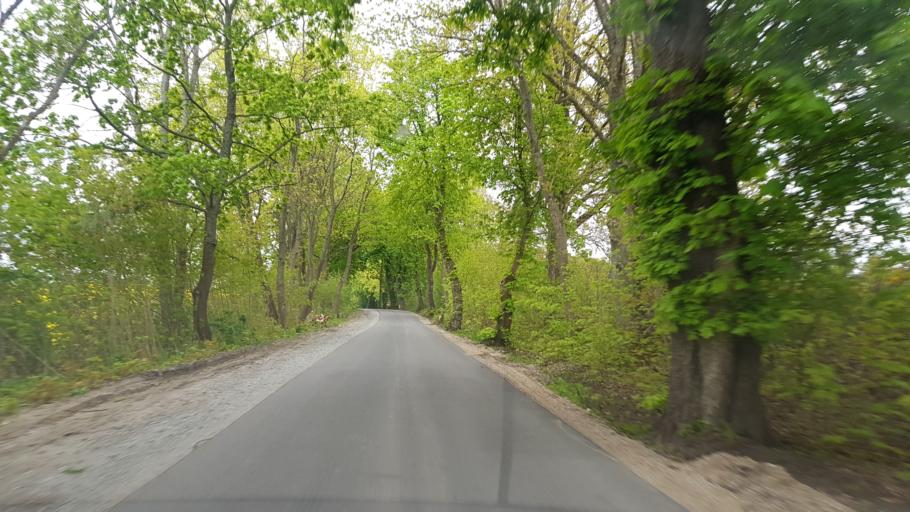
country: PL
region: West Pomeranian Voivodeship
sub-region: Powiat slawienski
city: Slawno
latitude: 54.2627
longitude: 16.5502
